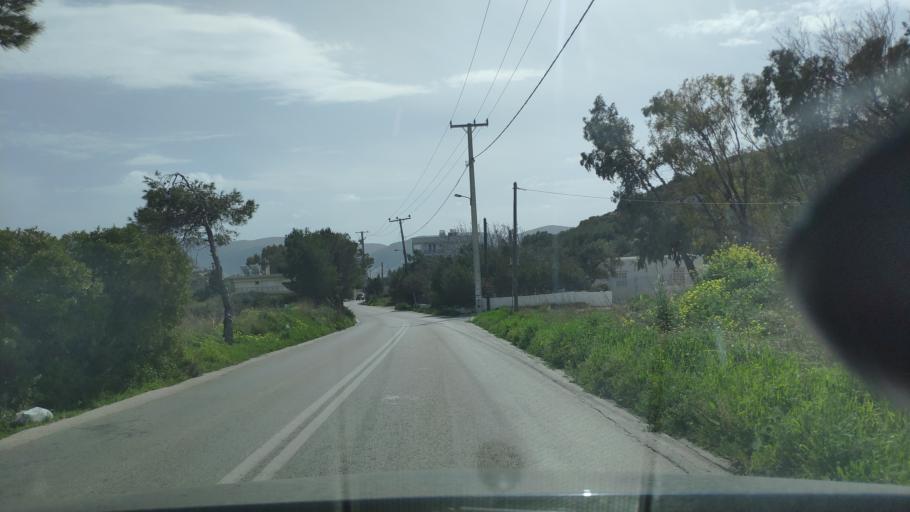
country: GR
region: Attica
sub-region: Nomarchia Anatolikis Attikis
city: Limin Mesoyaias
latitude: 37.8980
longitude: 24.0239
